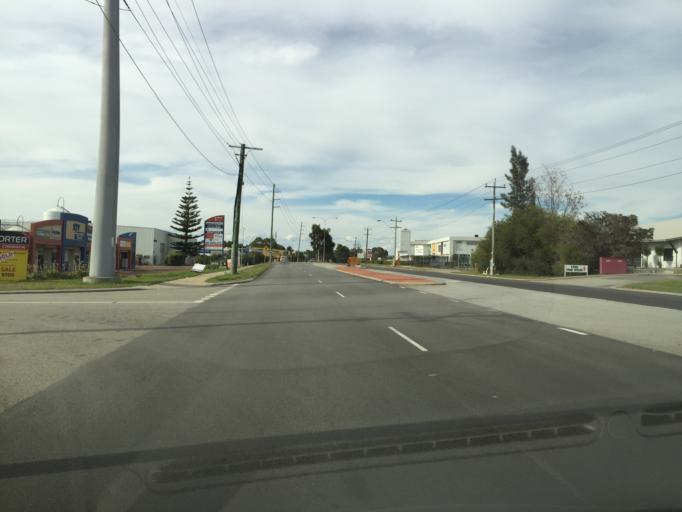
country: AU
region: Western Australia
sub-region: Canning
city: Canning Vale
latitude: -32.0616
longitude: 115.9052
